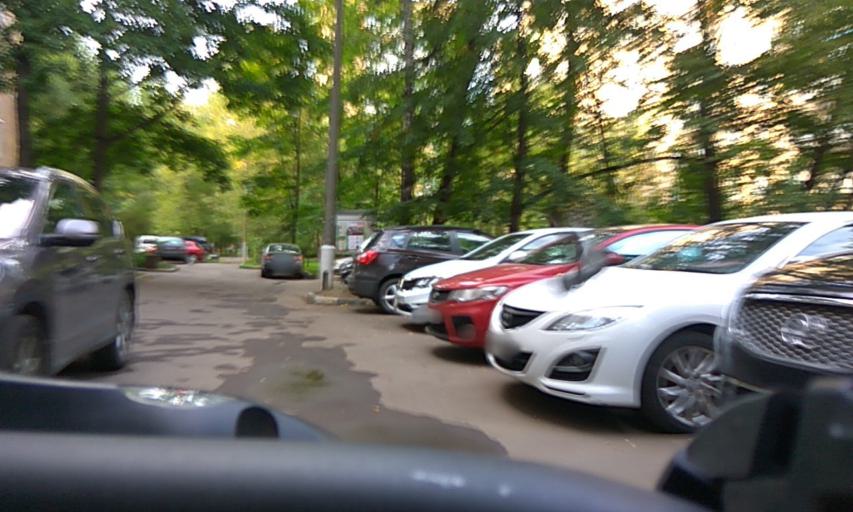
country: RU
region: Moscow
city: Kolomenskoye
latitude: 55.6866
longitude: 37.6914
